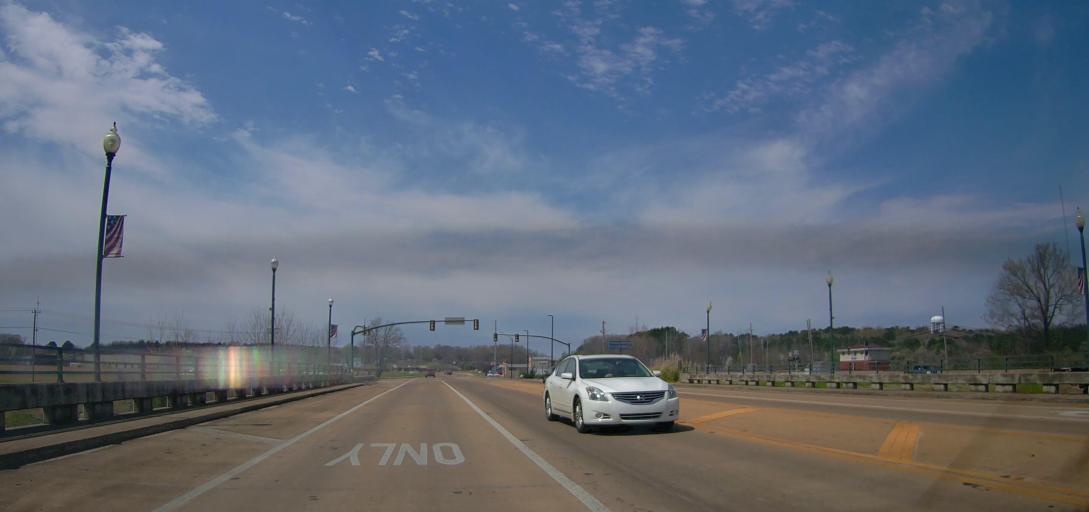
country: US
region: Mississippi
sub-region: Union County
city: New Albany
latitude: 34.4951
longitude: -89.0133
